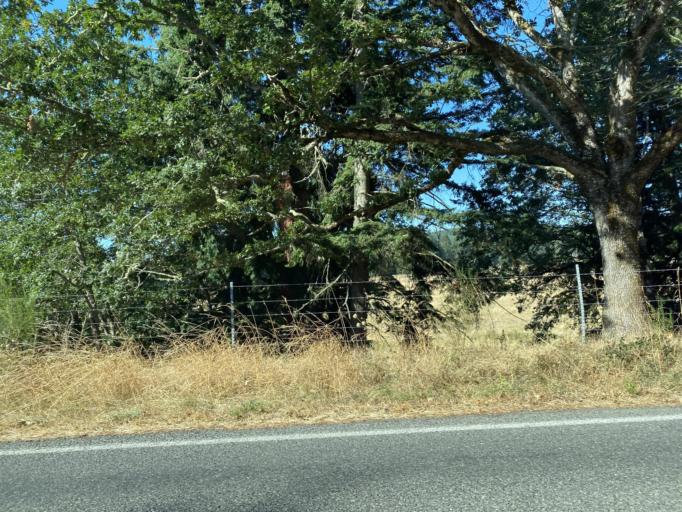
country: US
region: Washington
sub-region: Thurston County
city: Rainier
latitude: 46.8947
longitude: -122.7537
